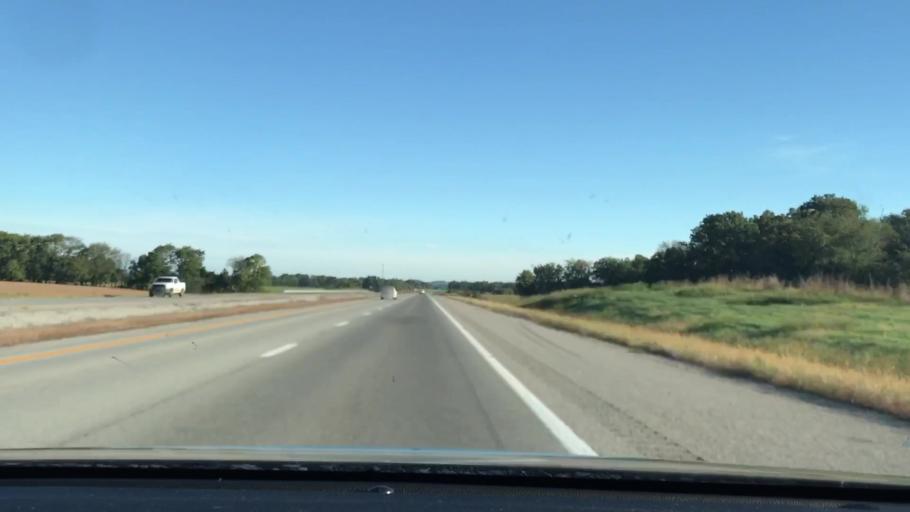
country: US
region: Kentucky
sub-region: Christian County
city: Hopkinsville
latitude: 36.7912
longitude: -87.4950
